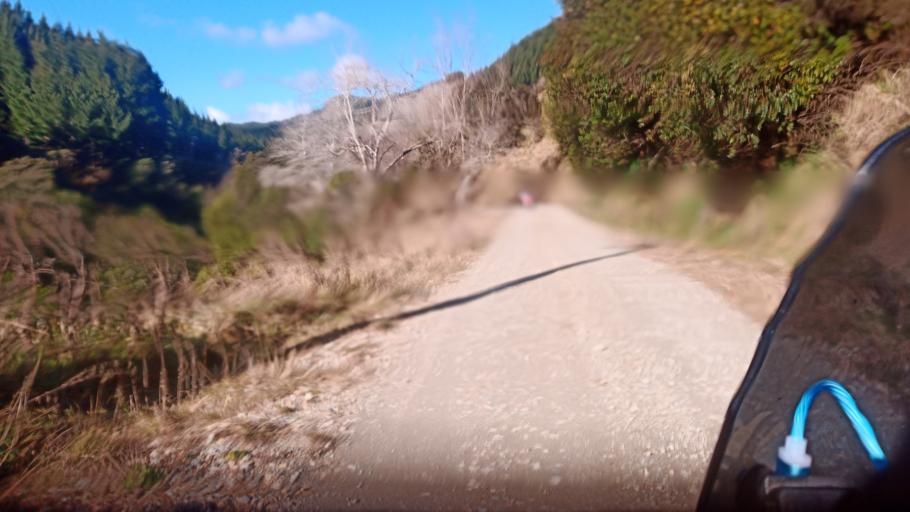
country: NZ
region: Hawke's Bay
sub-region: Wairoa District
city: Wairoa
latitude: -38.6601
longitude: 177.5007
